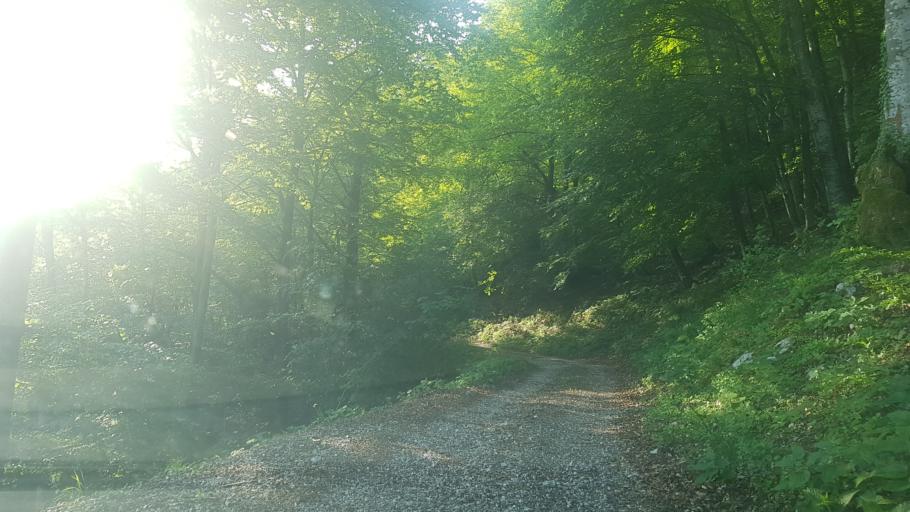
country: IT
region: Friuli Venezia Giulia
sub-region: Provincia di Udine
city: Cavazzo Carnico
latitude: 46.3485
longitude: 13.0268
